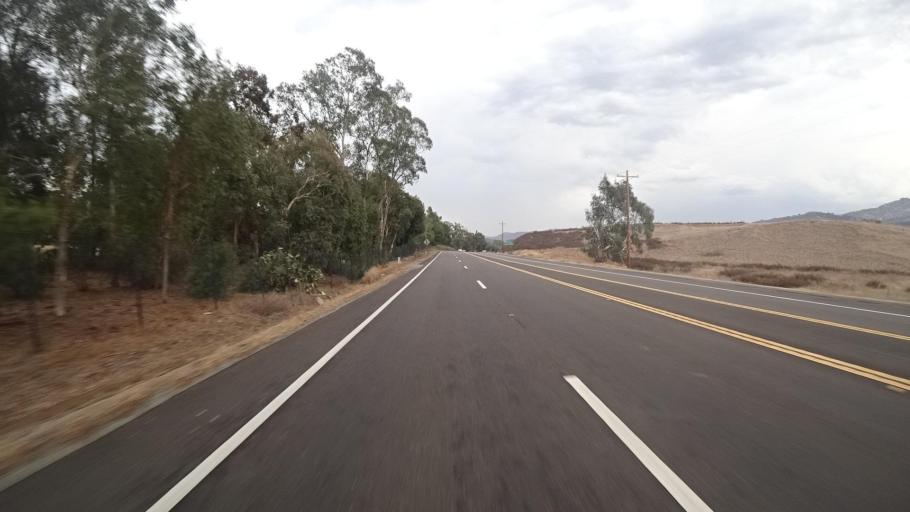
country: US
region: California
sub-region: San Diego County
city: San Pasqual
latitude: 33.0958
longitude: -117.0079
